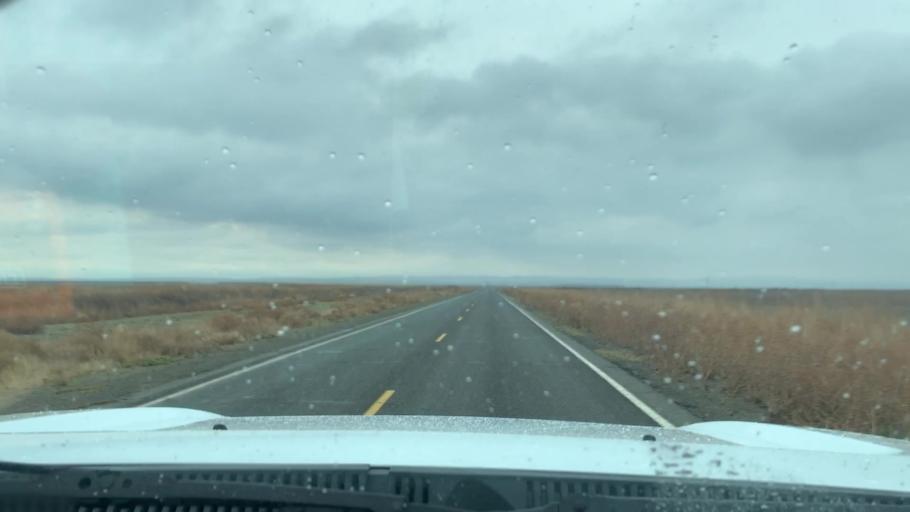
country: US
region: California
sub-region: Kings County
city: Kettleman City
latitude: 35.9340
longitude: -119.8222
